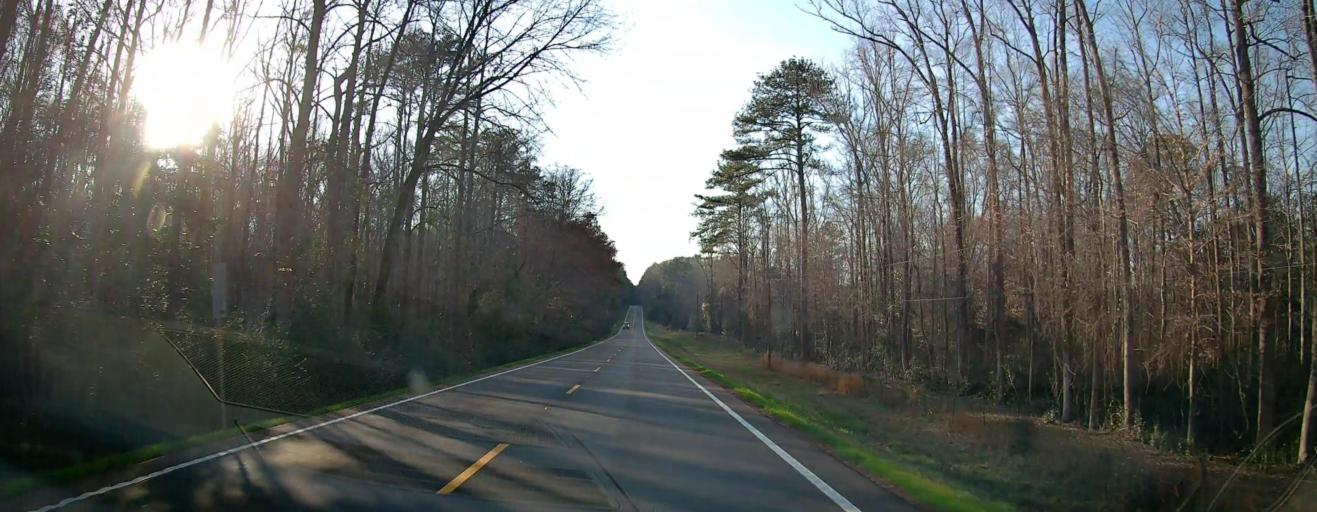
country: US
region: Georgia
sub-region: Harris County
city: Hamilton
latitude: 32.7487
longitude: -84.9181
